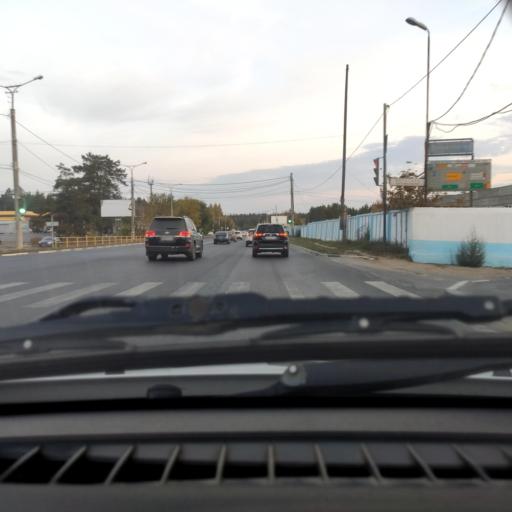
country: RU
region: Samara
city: Zhigulevsk
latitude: 53.4961
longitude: 49.4735
